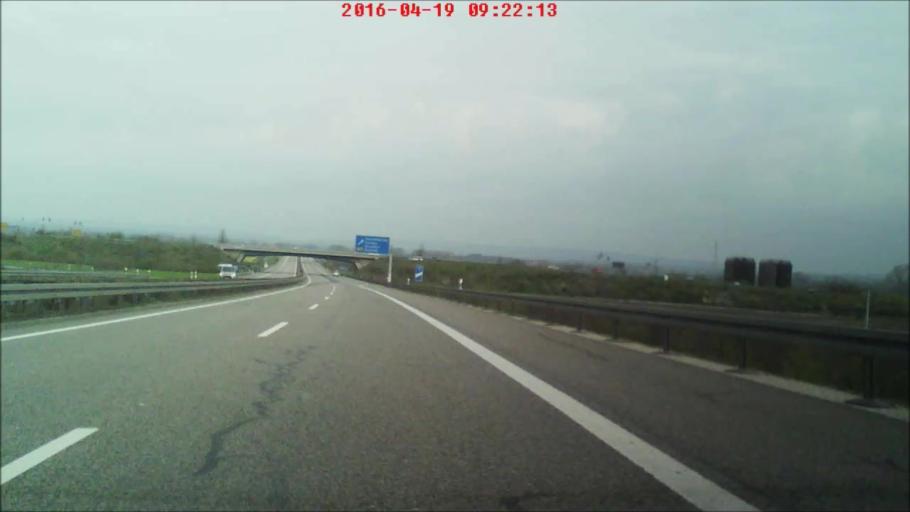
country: DE
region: Thuringia
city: Sprotau
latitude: 51.1498
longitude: 11.1737
